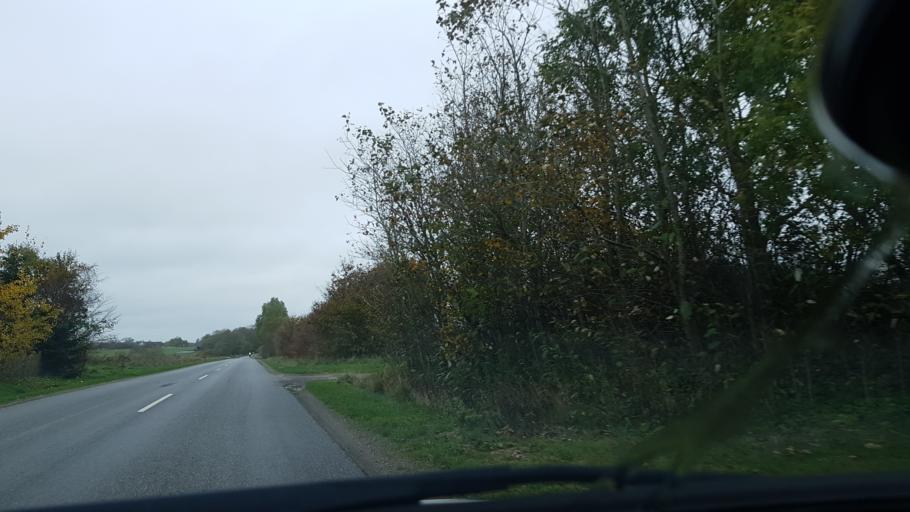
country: DK
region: South Denmark
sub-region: Tonder Kommune
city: Sherrebek
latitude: 55.2400
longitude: 8.8323
